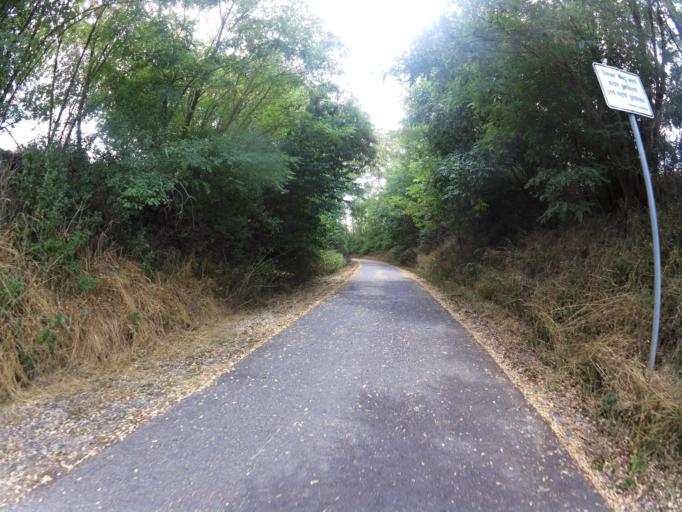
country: DE
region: Bavaria
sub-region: Regierungsbezirk Unterfranken
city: Sonderhofen
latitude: 49.5992
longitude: 10.0018
